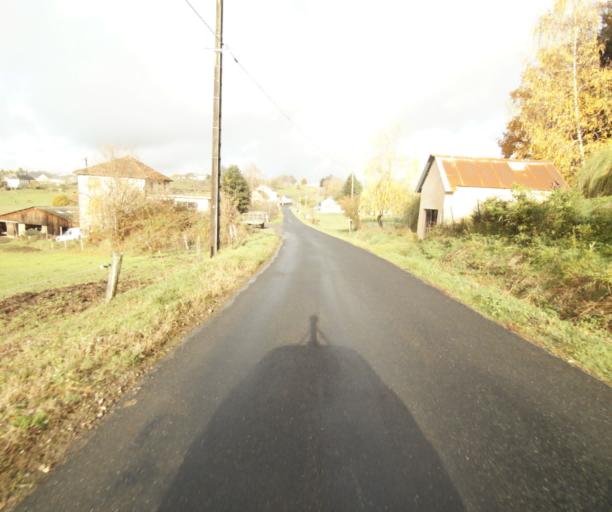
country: FR
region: Limousin
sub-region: Departement de la Correze
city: Cornil
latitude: 45.2113
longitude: 1.6429
